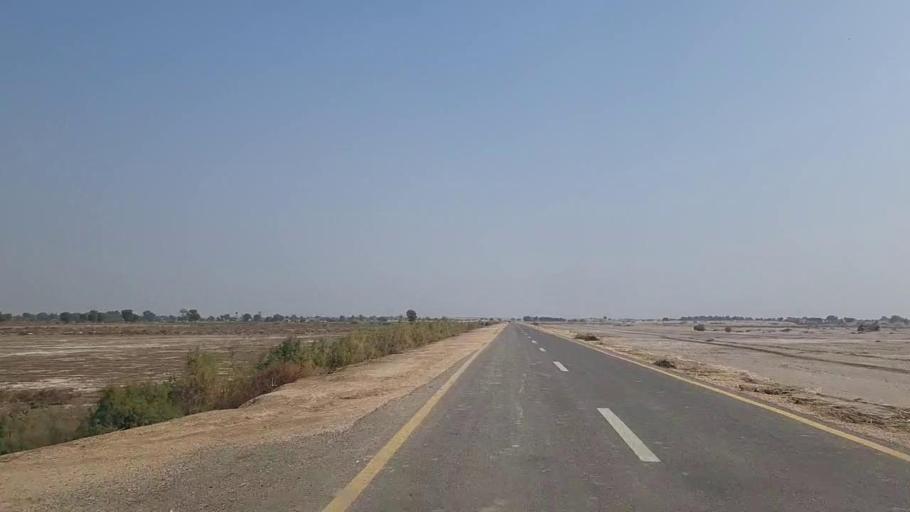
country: PK
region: Sindh
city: Jam Sahib
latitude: 26.3723
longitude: 68.5271
